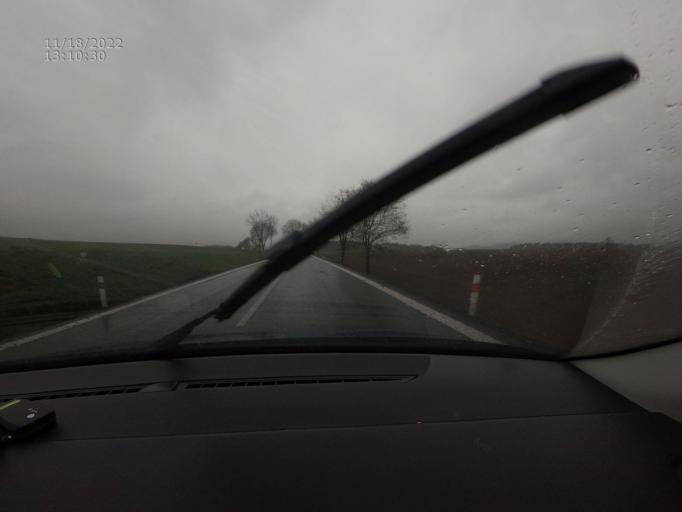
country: CZ
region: Plzensky
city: Hradek
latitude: 49.3309
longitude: 13.5634
